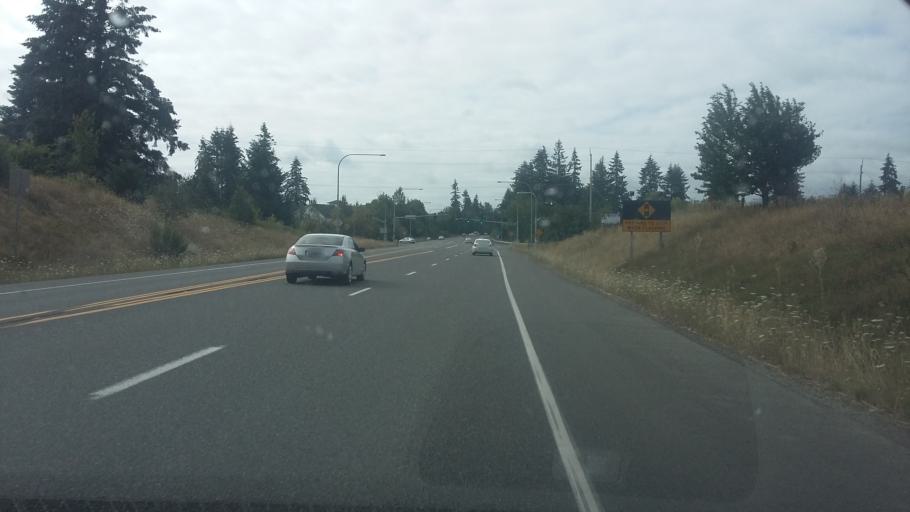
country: US
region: Washington
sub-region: Clark County
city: Battle Ground
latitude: 45.8007
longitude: -122.5491
